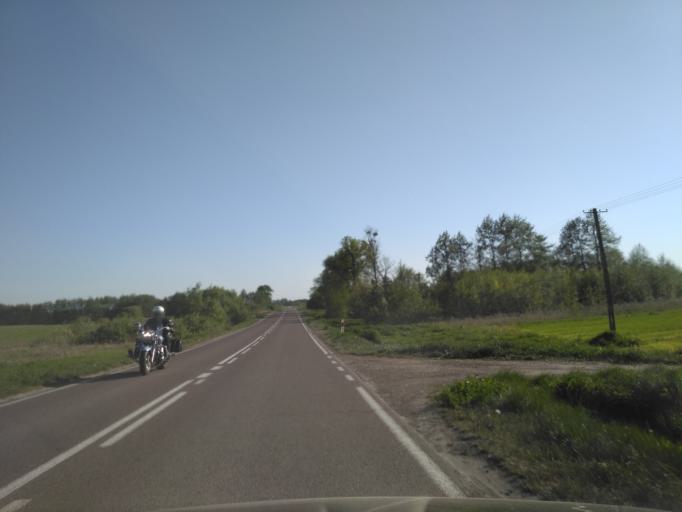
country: PL
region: Lublin Voivodeship
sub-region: Powiat swidnicki
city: Trawniki
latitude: 51.2029
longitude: 23.0666
